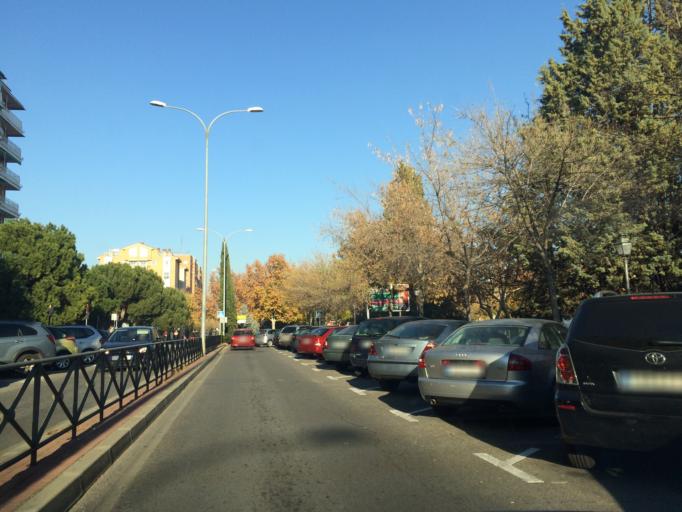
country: ES
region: Madrid
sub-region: Provincia de Madrid
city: Alcorcon
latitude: 40.3518
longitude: -3.8139
